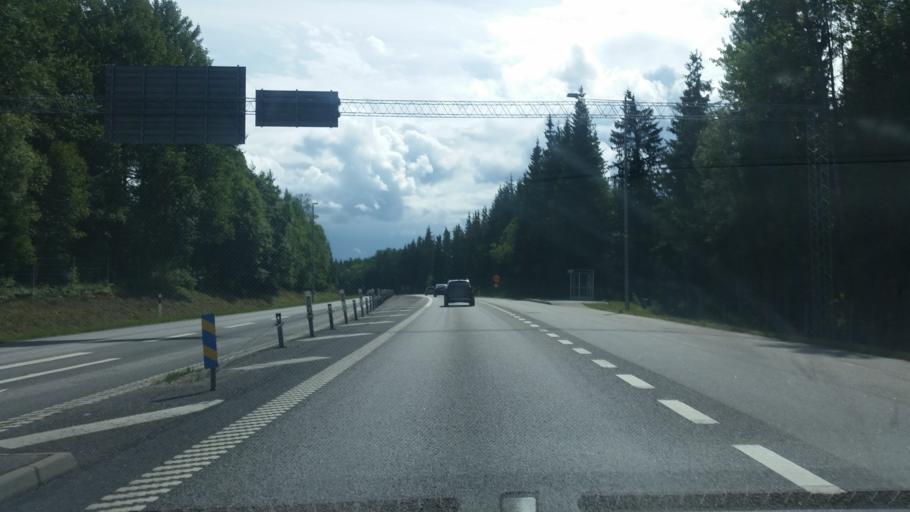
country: SE
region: Joenkoeping
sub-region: Mullsjo Kommun
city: Mullsjoe
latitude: 57.7670
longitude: 13.7226
